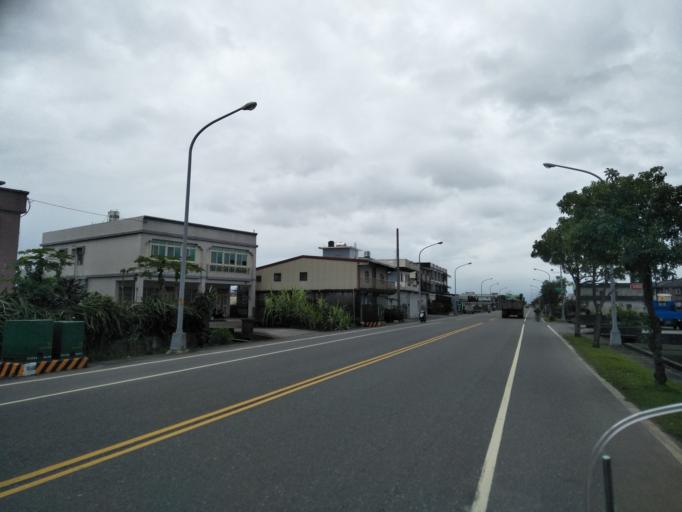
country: TW
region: Taiwan
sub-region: Yilan
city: Yilan
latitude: 24.7923
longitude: 121.7845
